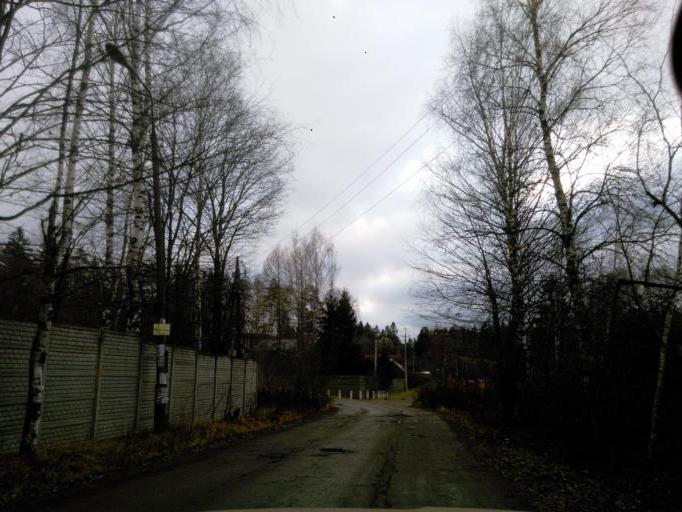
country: RU
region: Moskovskaya
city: Lozhki
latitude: 56.0546
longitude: 37.0979
